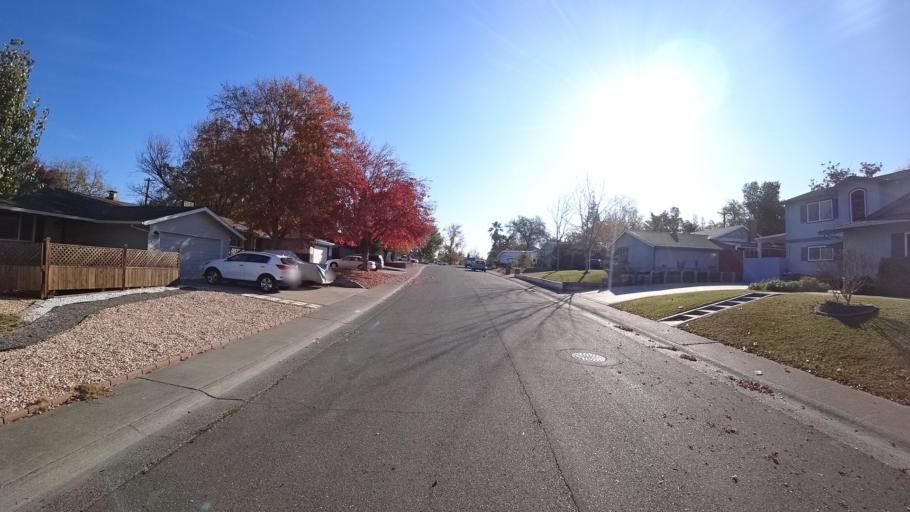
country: US
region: California
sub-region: Sacramento County
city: Fair Oaks
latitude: 38.6659
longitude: -121.2965
